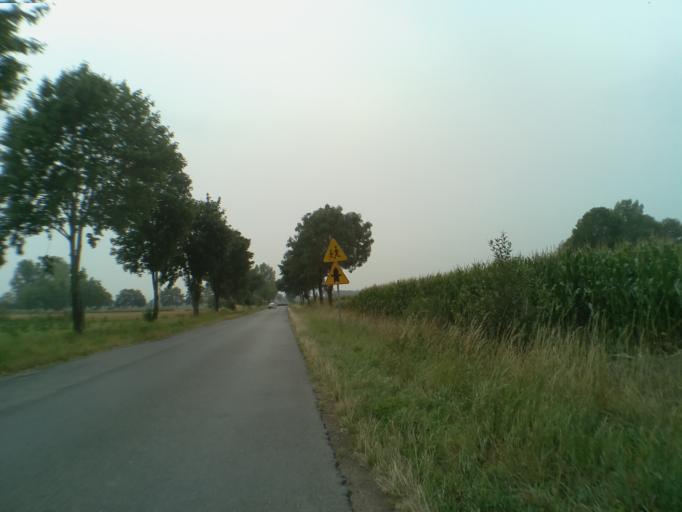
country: PL
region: Lower Silesian Voivodeship
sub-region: Powiat swidnicki
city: Stanowice
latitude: 50.9152
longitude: 16.3212
